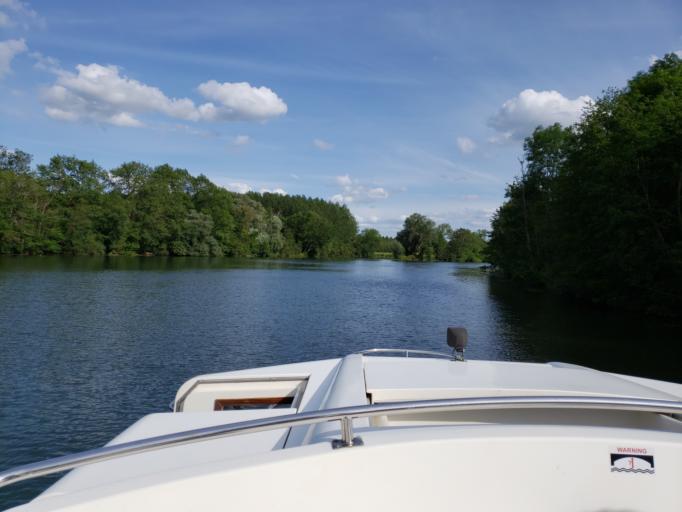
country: FR
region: Bourgogne
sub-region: Departement de l'Yonne
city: Migennes
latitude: 47.9539
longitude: 3.5061
